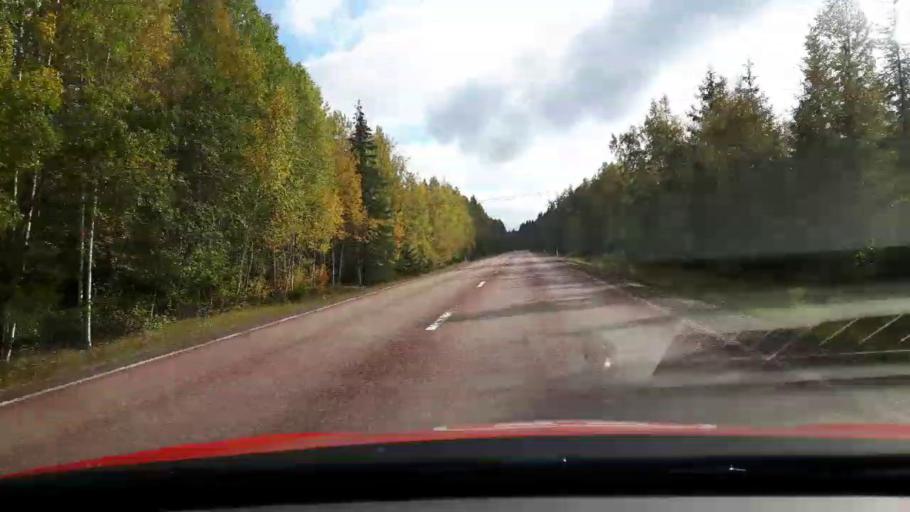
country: SE
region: Gaevleborg
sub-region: Ljusdals Kommun
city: Jaervsoe
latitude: 61.6416
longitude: 16.2299
